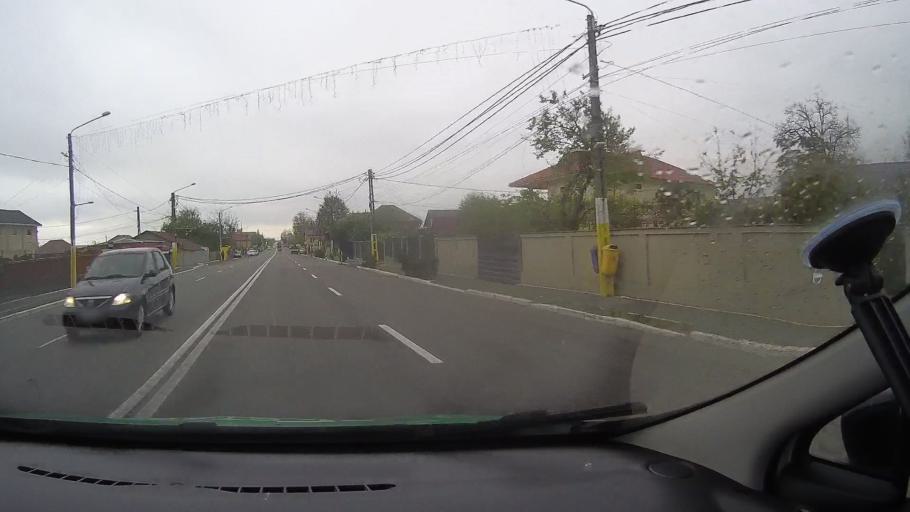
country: RO
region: Constanta
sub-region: Comuna Valu lui Traian
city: Valu lui Traian
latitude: 44.1649
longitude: 28.4893
